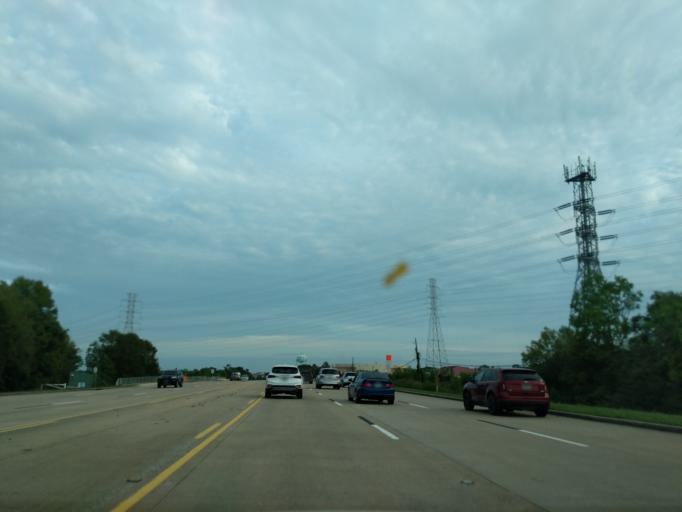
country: US
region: Texas
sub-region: Harris County
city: Nassau Bay
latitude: 29.5297
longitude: -95.0909
